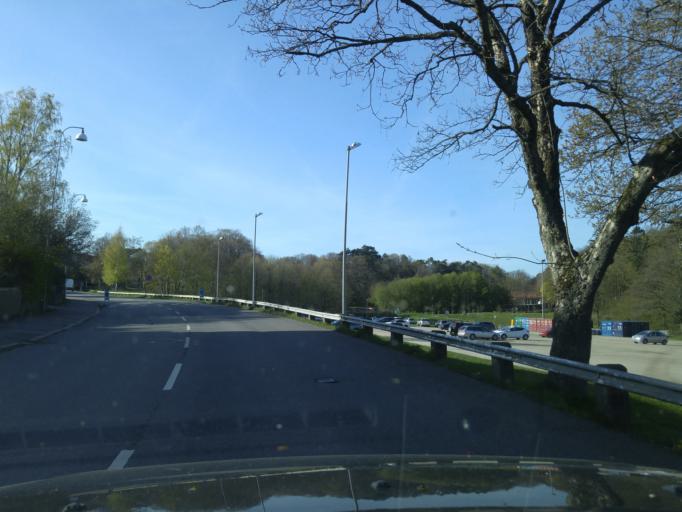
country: SE
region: Vaestra Goetaland
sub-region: Goteborg
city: Majorna
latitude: 57.6805
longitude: 11.9355
